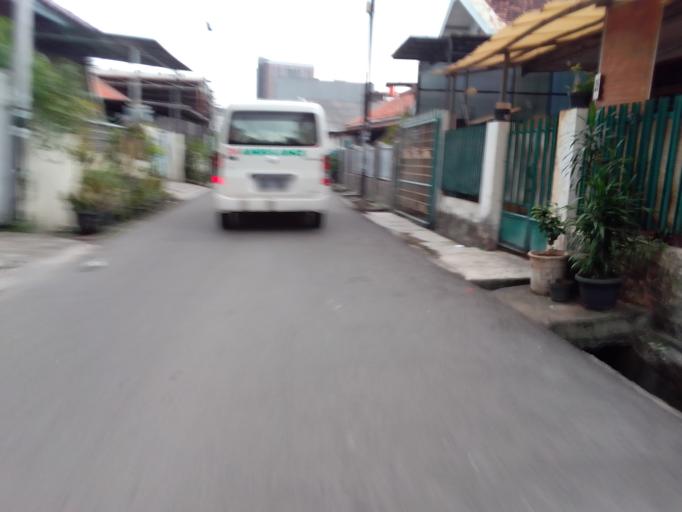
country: ID
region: Jakarta Raya
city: Jakarta
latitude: -6.1746
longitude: 106.8144
